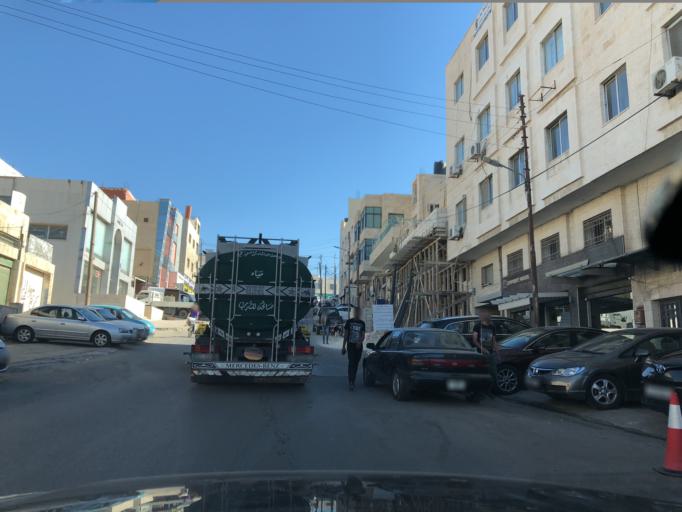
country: JO
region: Amman
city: Wadi as Sir
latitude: 31.9444
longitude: 35.8474
